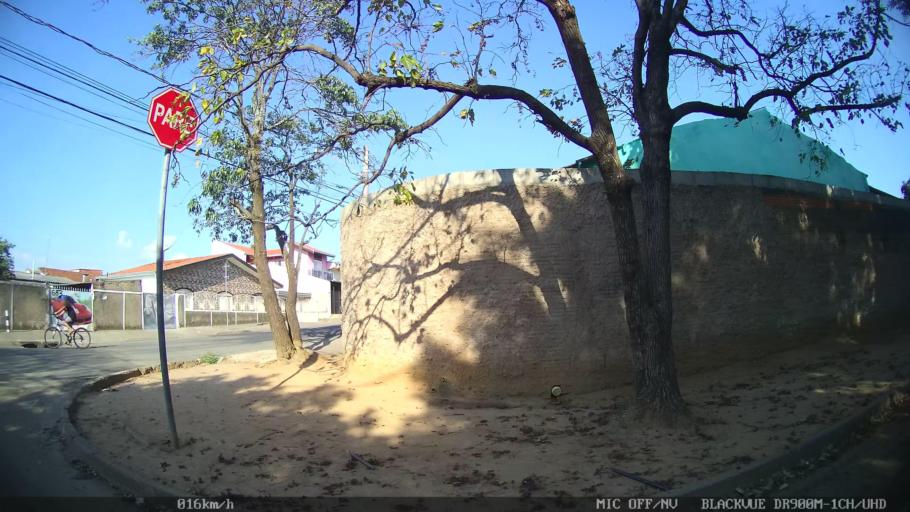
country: BR
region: Sao Paulo
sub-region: Indaiatuba
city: Indaiatuba
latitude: -22.9873
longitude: -47.1543
